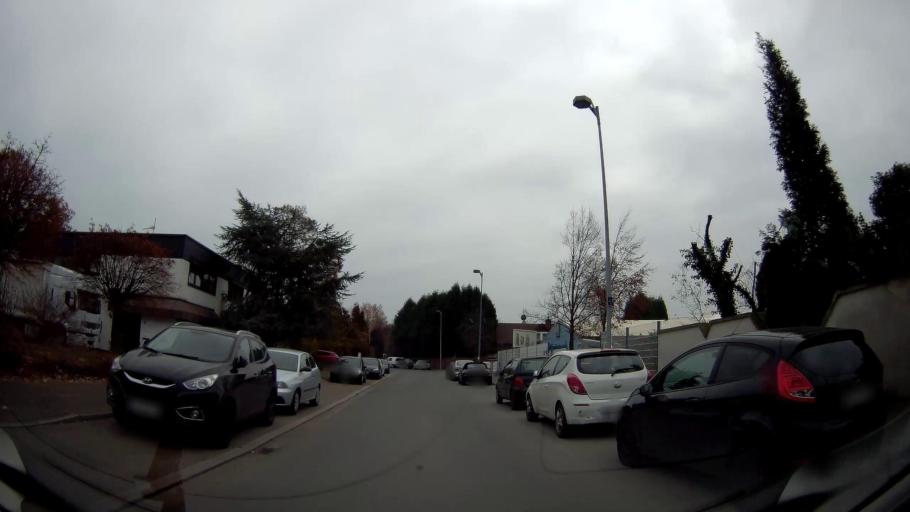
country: DE
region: North Rhine-Westphalia
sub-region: Regierungsbezirk Munster
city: Gladbeck
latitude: 51.5520
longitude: 7.0361
